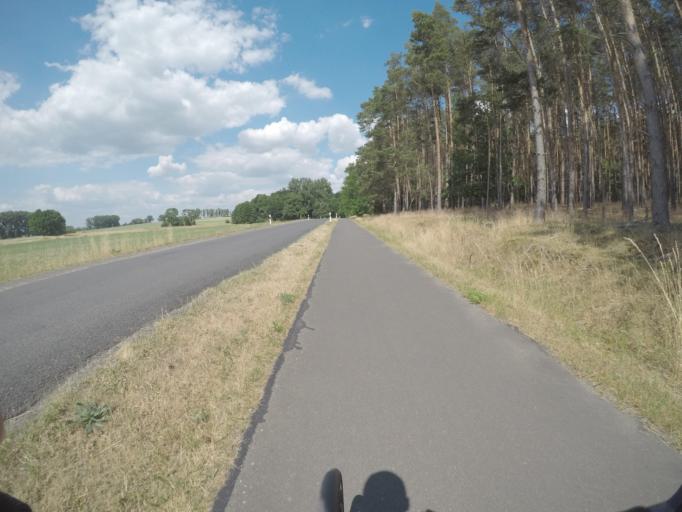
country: DE
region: Brandenburg
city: Roskow
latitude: 52.4371
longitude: 12.7123
